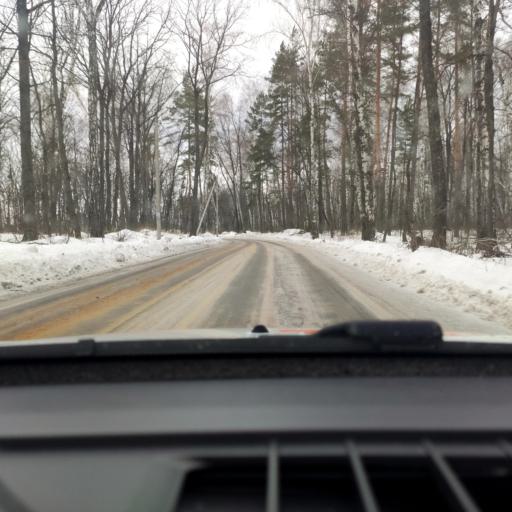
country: RU
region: Voronezj
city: Podgornoye
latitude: 51.7534
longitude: 39.1535
